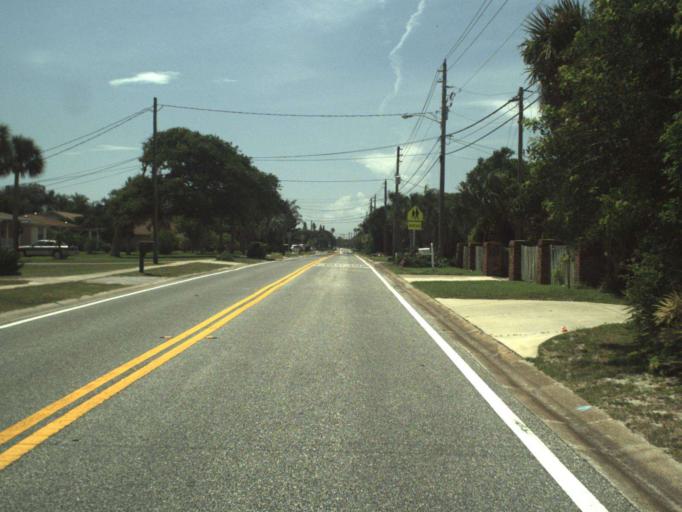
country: US
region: Florida
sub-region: Volusia County
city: Daytona Beach Shores
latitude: 29.1791
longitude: -80.9880
